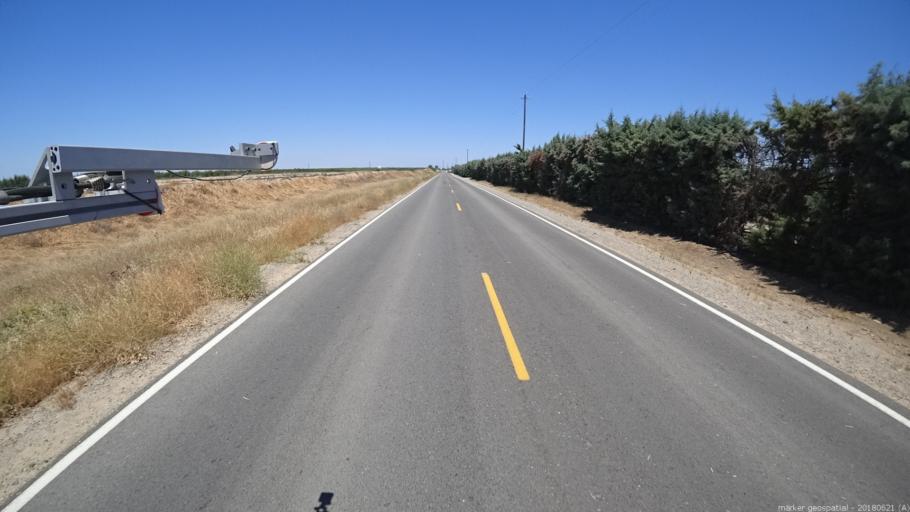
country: US
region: California
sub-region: Madera County
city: Bonadelle Ranchos-Madera Ranchos
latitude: 36.9012
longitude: -119.8938
